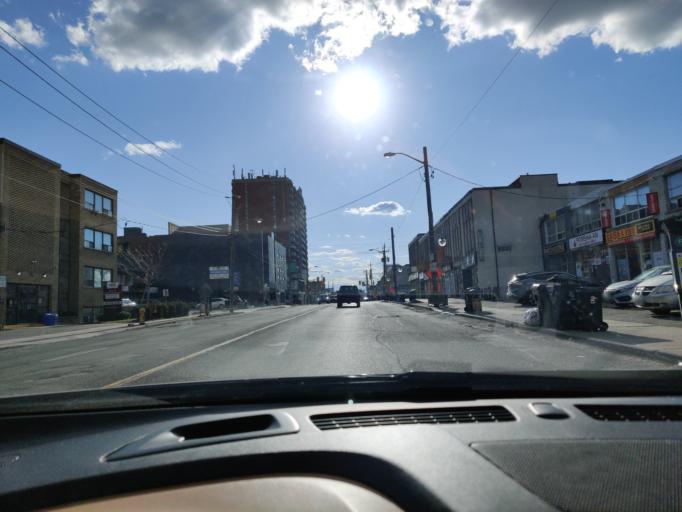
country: CA
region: Ontario
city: Toronto
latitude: 43.6966
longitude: -79.4460
